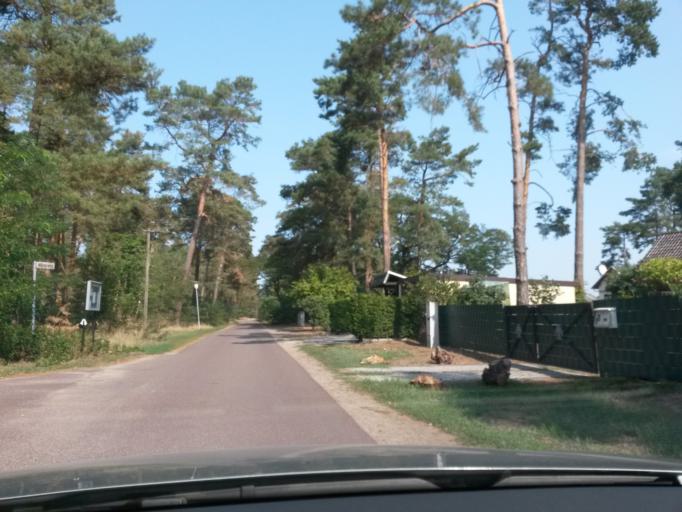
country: DE
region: Saxony-Anhalt
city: Hohenwarthe
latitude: 52.2344
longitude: 11.7080
